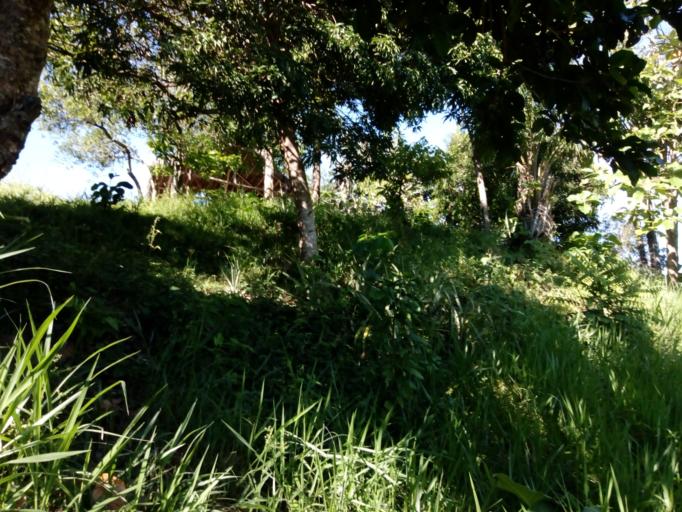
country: CO
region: Boyaca
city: Puerto Boyaca
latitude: 6.0022
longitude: -74.3727
